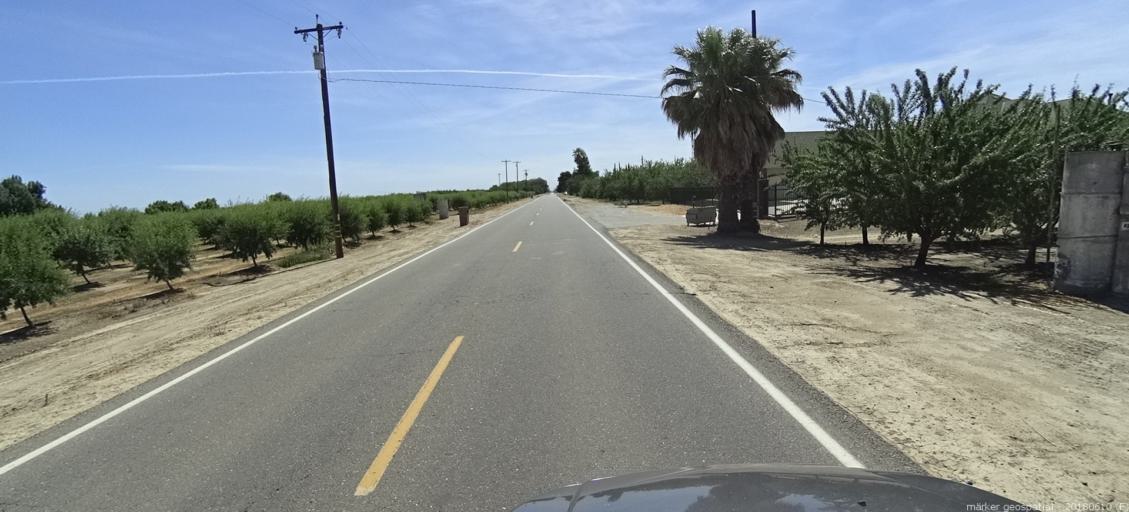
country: US
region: California
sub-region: Madera County
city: Chowchilla
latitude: 37.0182
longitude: -120.3227
